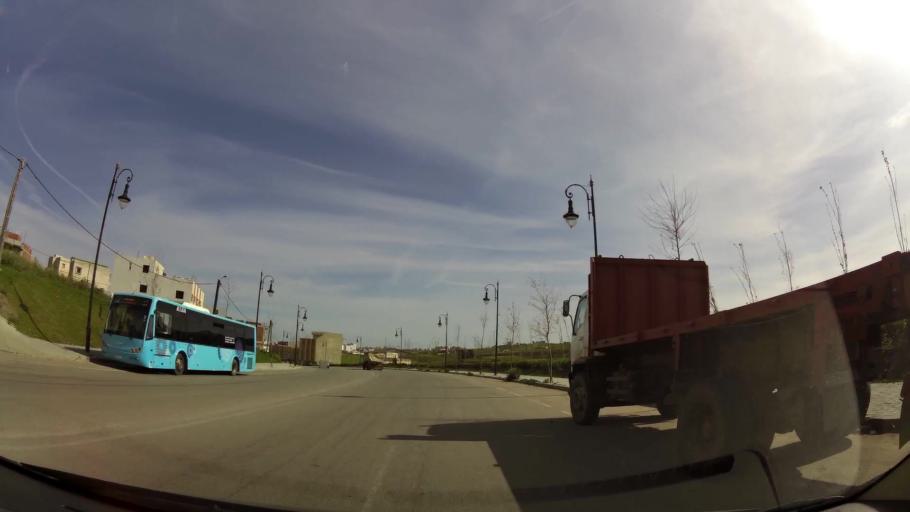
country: MA
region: Tanger-Tetouan
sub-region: Tanger-Assilah
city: Tangier
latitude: 35.7099
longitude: -5.8049
